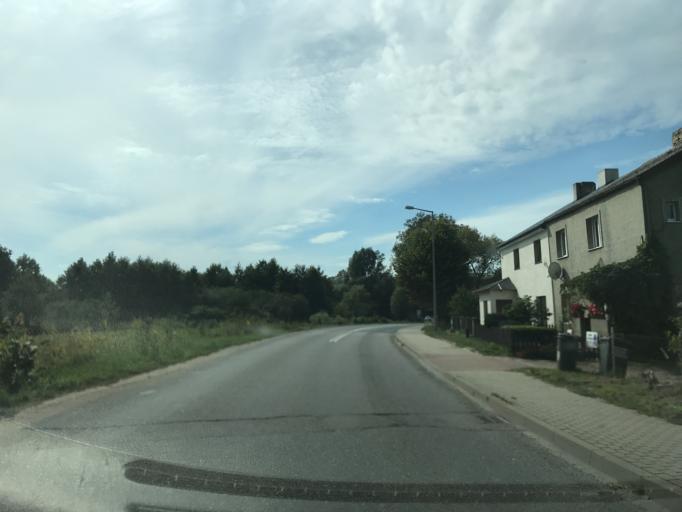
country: PL
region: Pomeranian Voivodeship
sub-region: Powiat pucki
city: Krokowa
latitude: 54.7809
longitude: 18.1687
